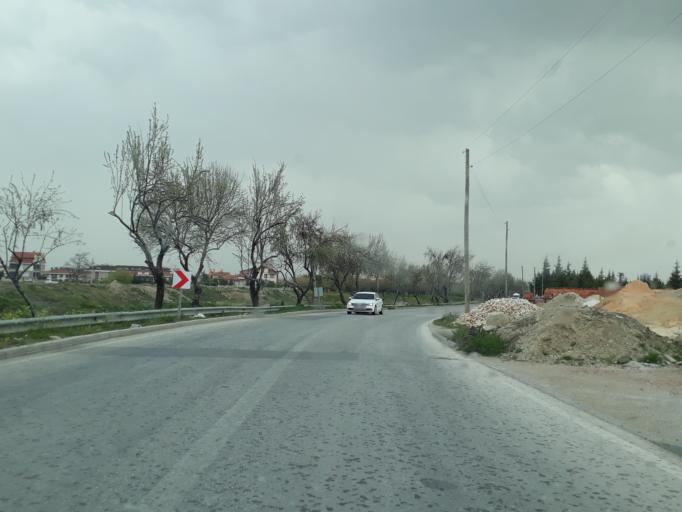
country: TR
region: Konya
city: Selcuklu
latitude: 37.9190
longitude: 32.4710
